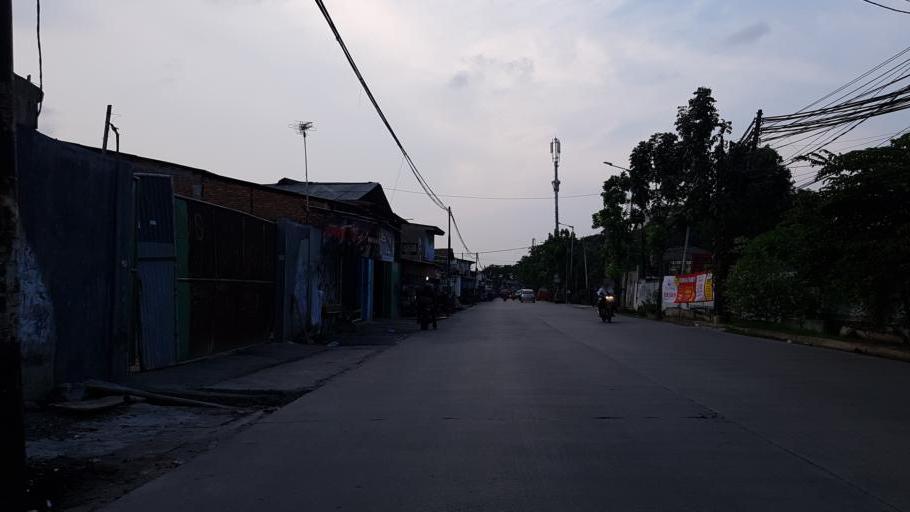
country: ID
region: West Java
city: Teluknaga
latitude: -6.1282
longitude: 106.7408
